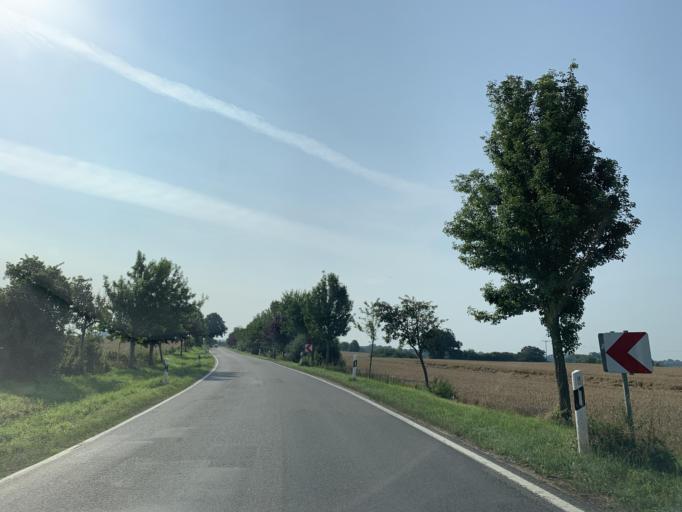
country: DE
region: Mecklenburg-Vorpommern
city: Blankensee
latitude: 53.4169
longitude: 13.2178
